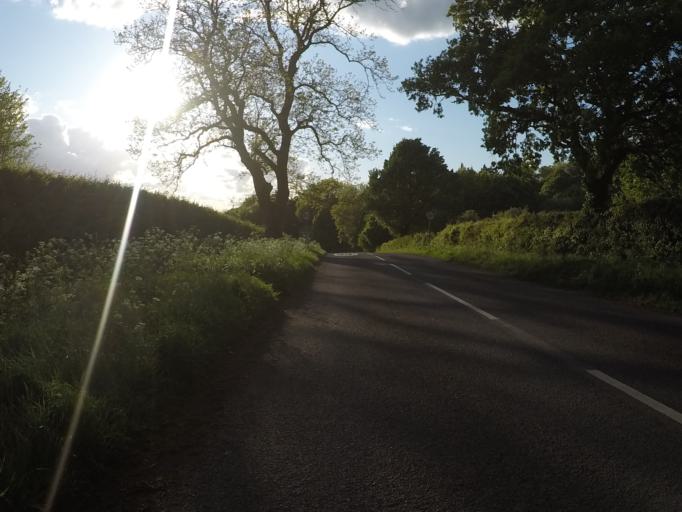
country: GB
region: England
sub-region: Oxfordshire
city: Charlbury
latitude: 51.8679
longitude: -1.4653
